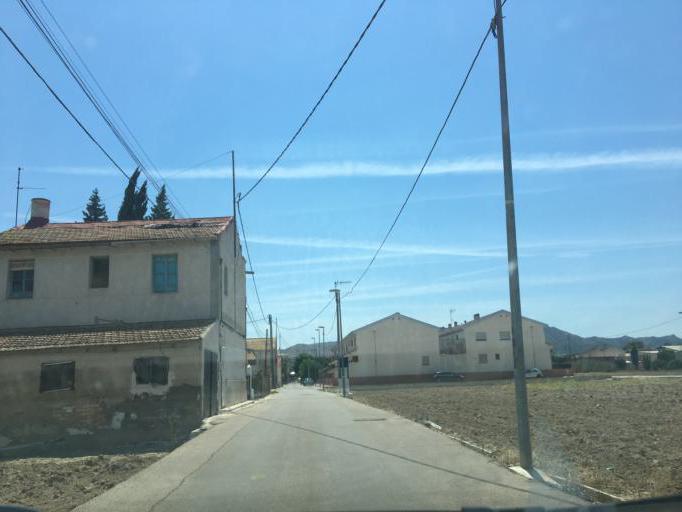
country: ES
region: Murcia
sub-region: Murcia
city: Santomera
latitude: 38.0178
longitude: -1.0552
